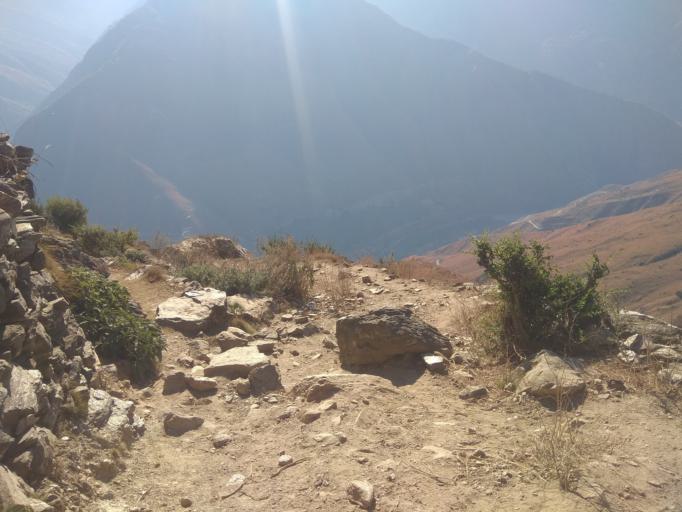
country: NP
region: Mid Western
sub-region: Karnali Zone
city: Jumla
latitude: 29.3128
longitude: 81.7408
